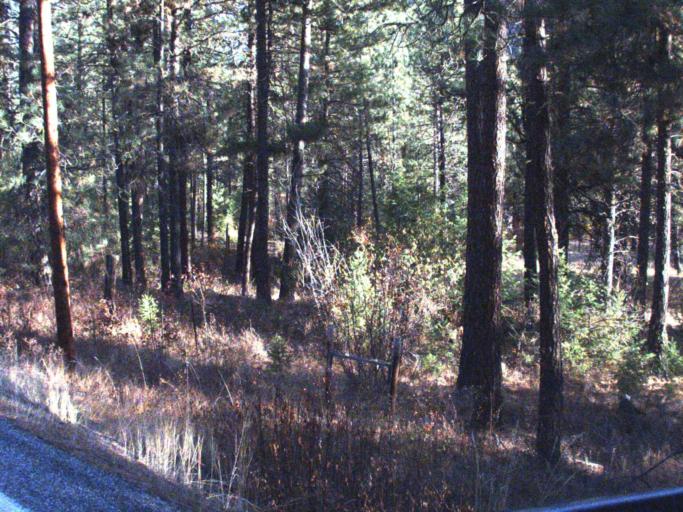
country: US
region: Washington
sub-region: Okanogan County
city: Coulee Dam
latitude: 48.1947
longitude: -118.7129
